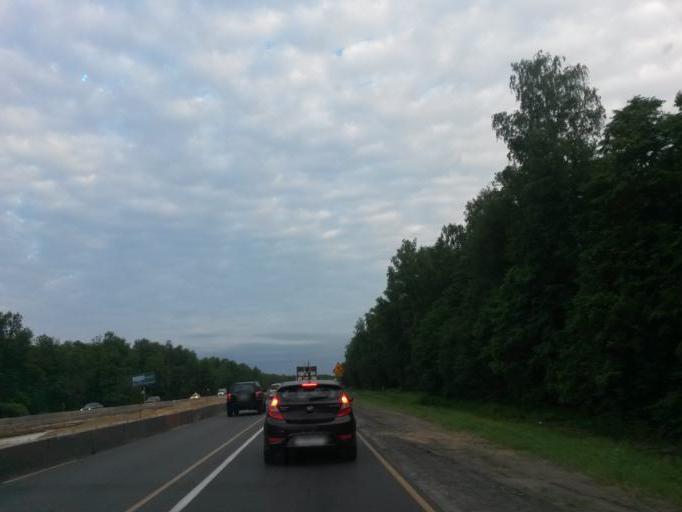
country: RU
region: Moskovskaya
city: Lyubuchany
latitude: 55.2187
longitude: 37.5332
